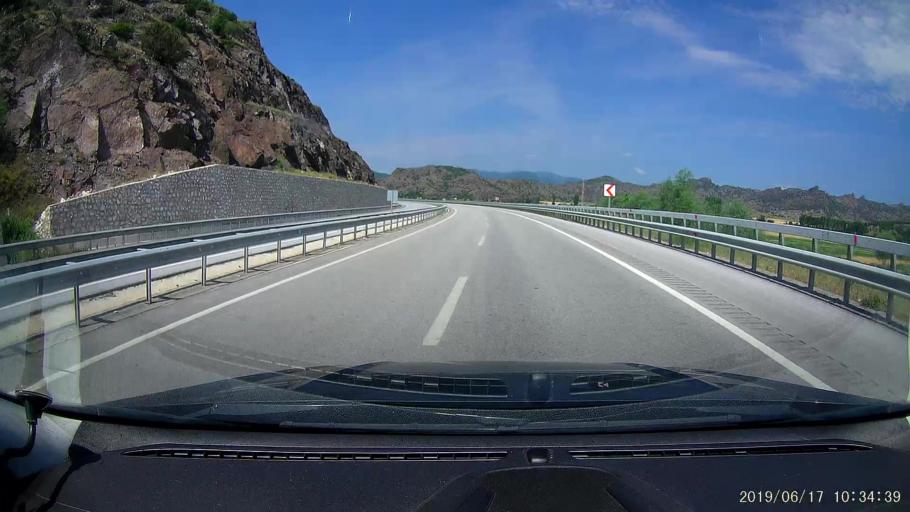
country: TR
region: Corum
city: Osmancik
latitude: 40.9815
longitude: 34.7196
